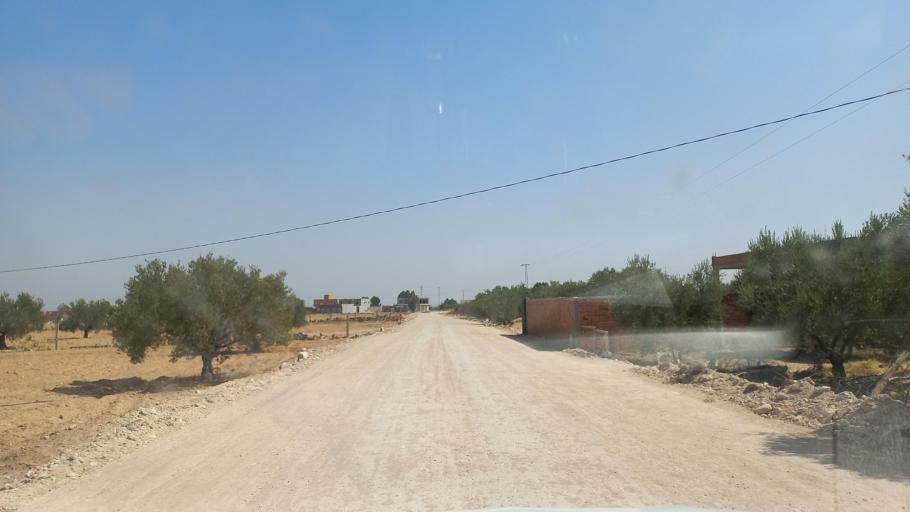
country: TN
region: Al Qasrayn
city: Kasserine
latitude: 35.2562
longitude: 9.0144
